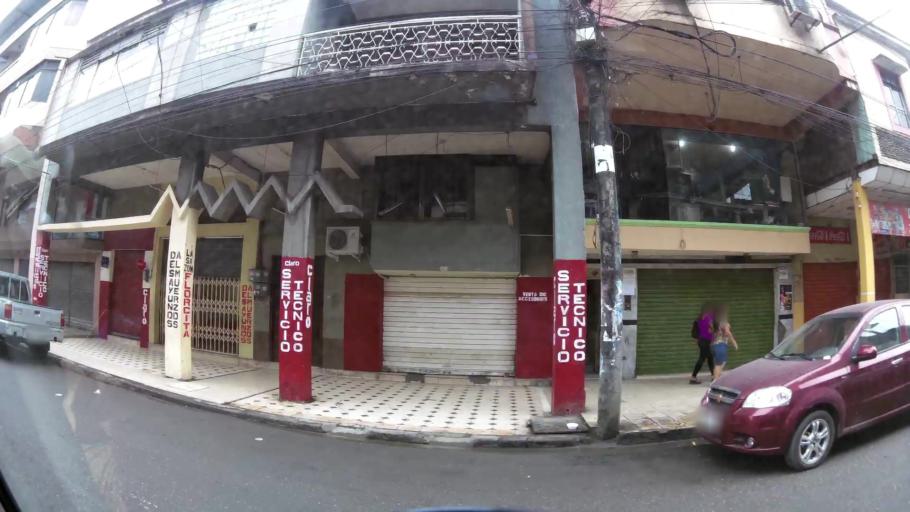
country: EC
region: El Oro
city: Pasaje
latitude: -3.3281
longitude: -79.8090
